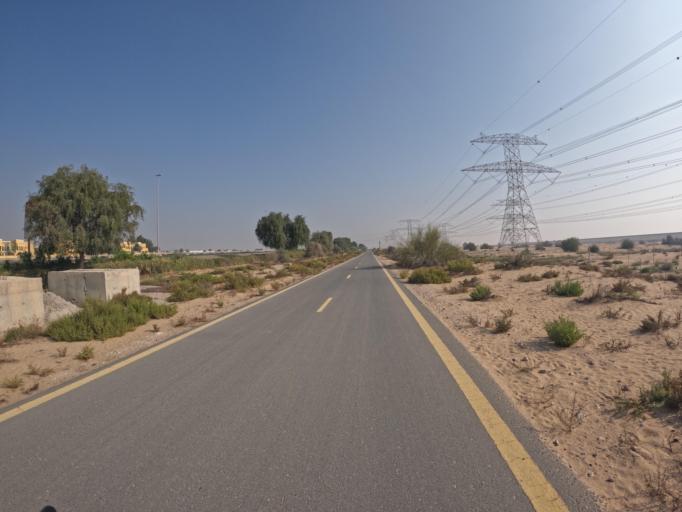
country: AE
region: Dubai
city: Dubai
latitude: 25.0290
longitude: 55.2892
